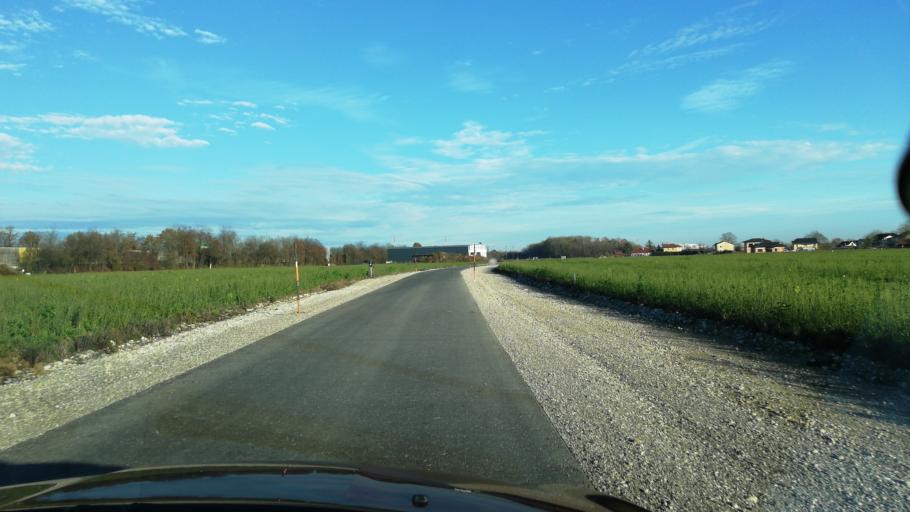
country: AT
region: Upper Austria
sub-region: Wels Stadt
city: Wels
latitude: 48.1891
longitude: 14.0355
